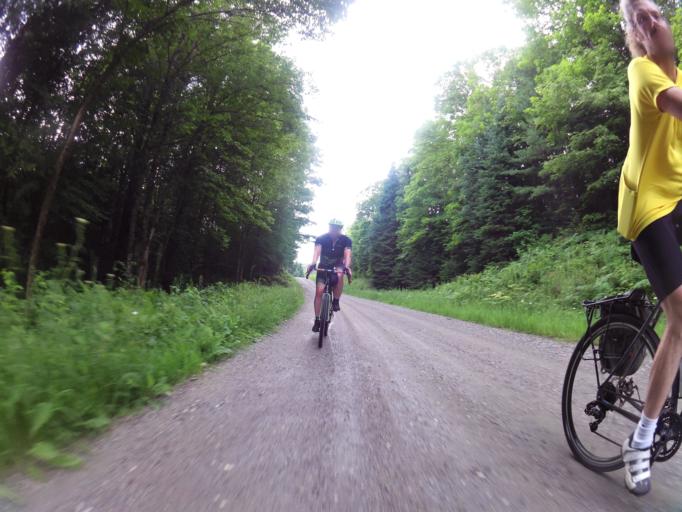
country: CA
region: Ontario
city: Renfrew
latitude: 45.0550
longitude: -76.7503
